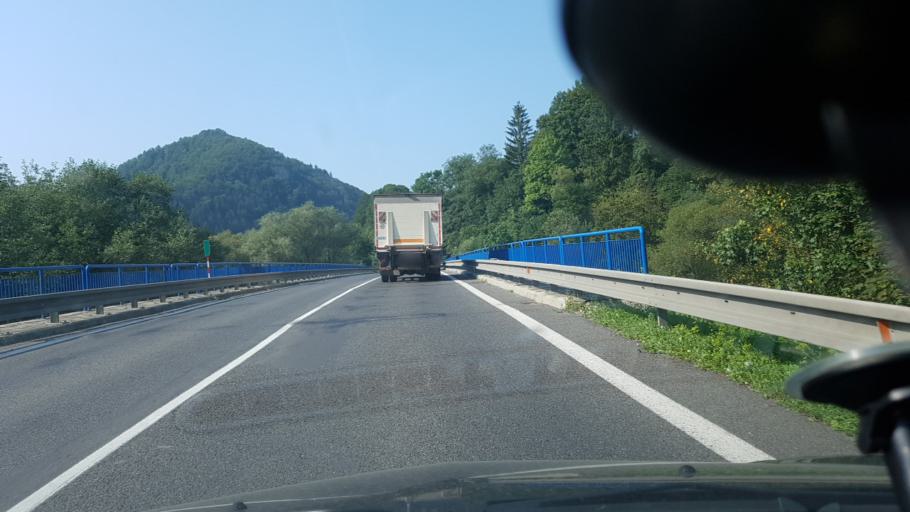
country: SK
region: Zilinsky
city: Tvrdosin
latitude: 49.2715
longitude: 19.4608
